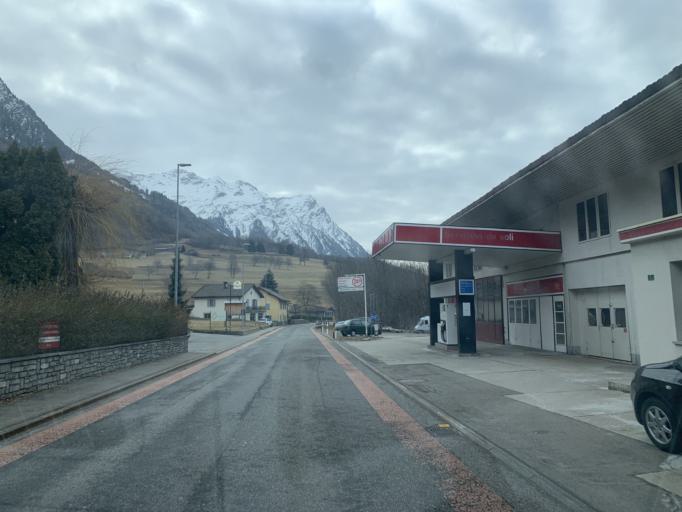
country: CH
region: Ticino
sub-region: Blenio District
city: Acquarossa
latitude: 46.5265
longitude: 8.9403
